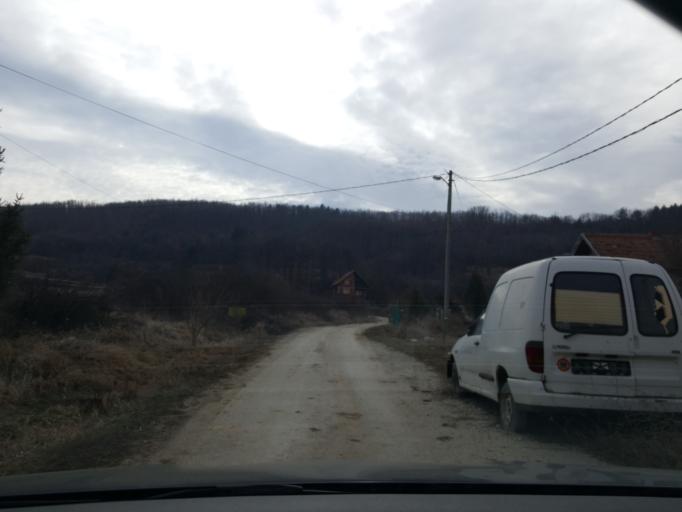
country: RS
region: Central Serbia
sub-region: Pirotski Okrug
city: Dimitrovgrad
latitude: 43.0079
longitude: 22.7511
